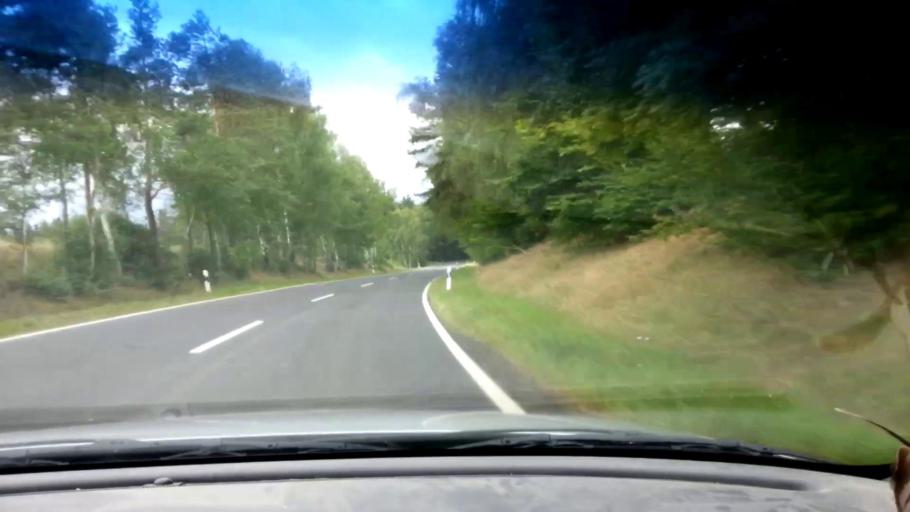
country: DE
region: Bavaria
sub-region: Upper Palatinate
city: Waldsassen
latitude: 50.0307
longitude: 12.3054
